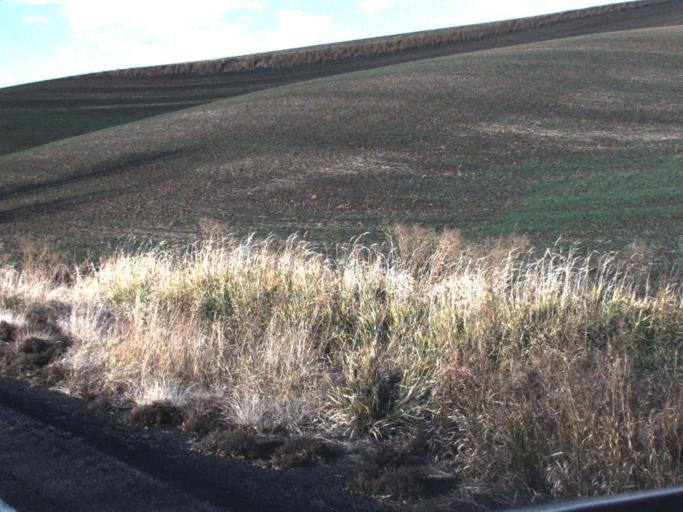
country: US
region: Washington
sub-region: Whitman County
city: Colfax
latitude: 46.7645
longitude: -117.4136
